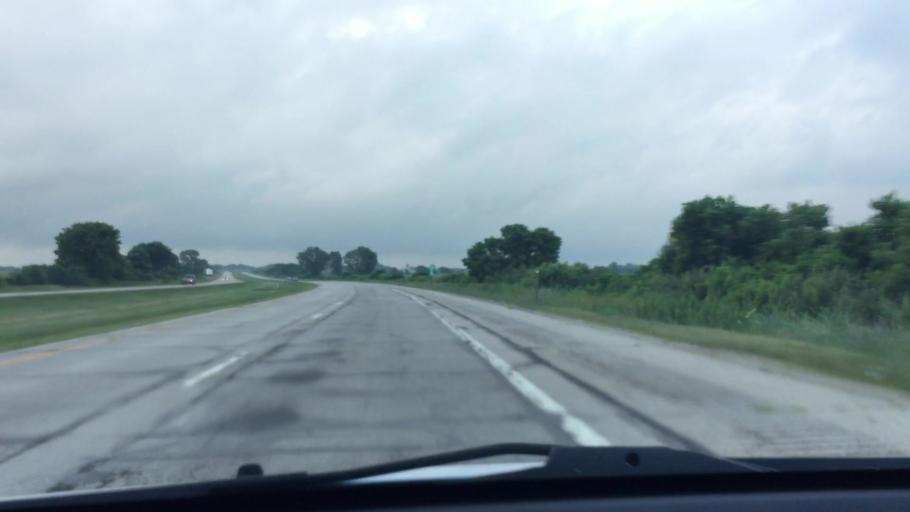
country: US
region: Wisconsin
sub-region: Walworth County
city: Como
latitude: 42.6446
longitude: -88.5002
